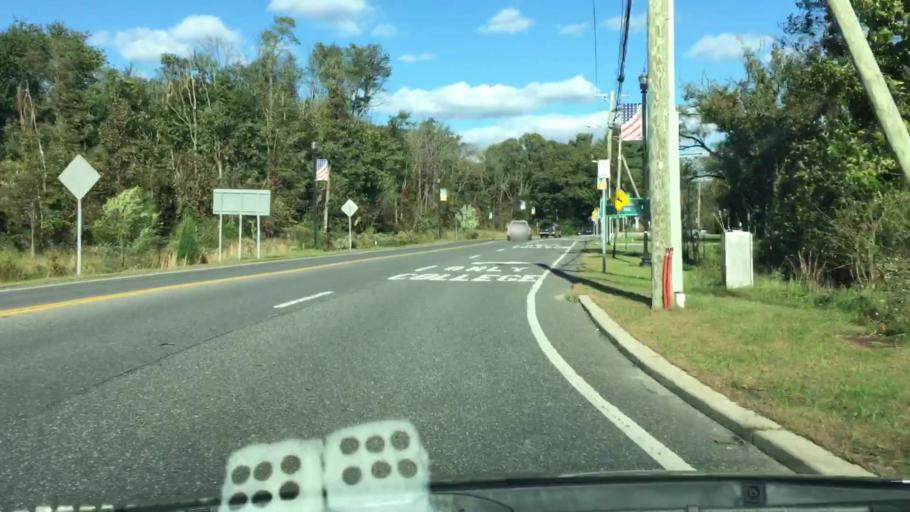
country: US
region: New Jersey
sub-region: Gloucester County
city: Turnersville
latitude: 39.7867
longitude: -75.0450
